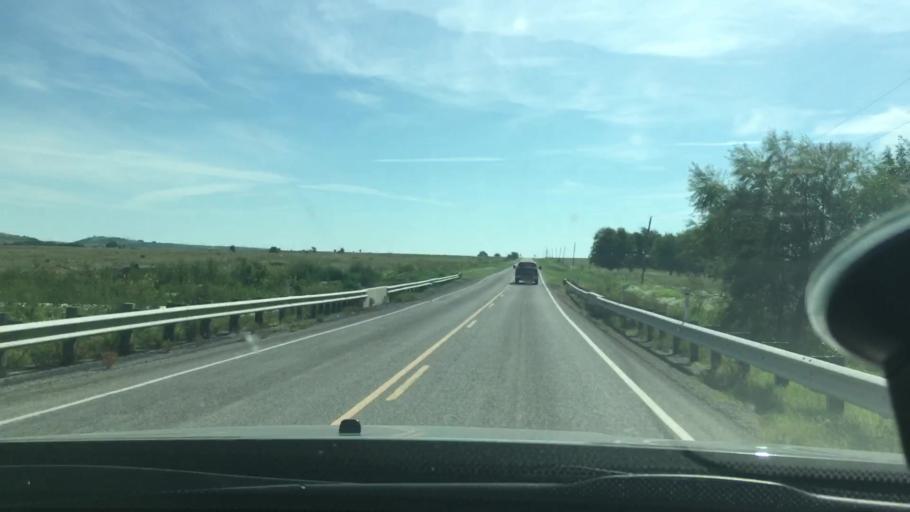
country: US
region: Oklahoma
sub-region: Carter County
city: Lone Grove
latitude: 34.3327
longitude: -97.2650
